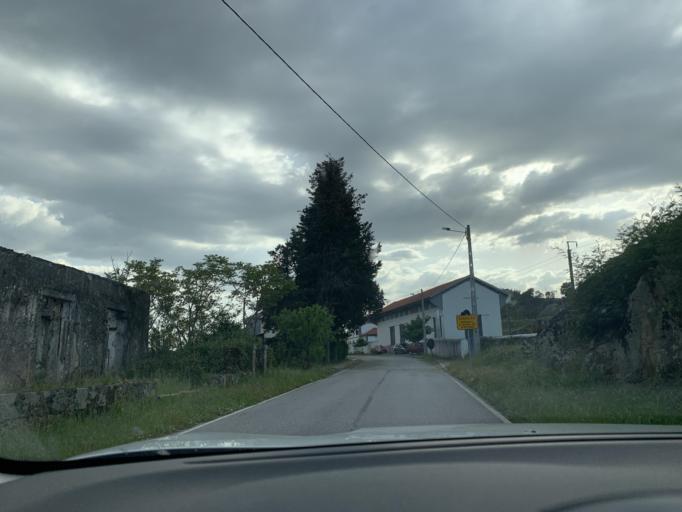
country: PT
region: Guarda
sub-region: Fornos de Algodres
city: Fornos de Algodres
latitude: 40.5739
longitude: -7.6006
